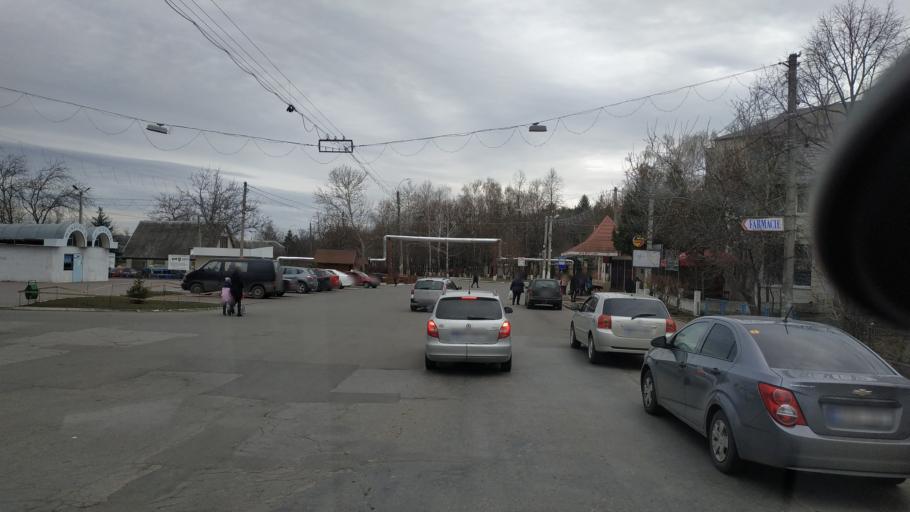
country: MD
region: Chisinau
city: Vadul lui Voda
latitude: 47.0879
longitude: 29.0795
